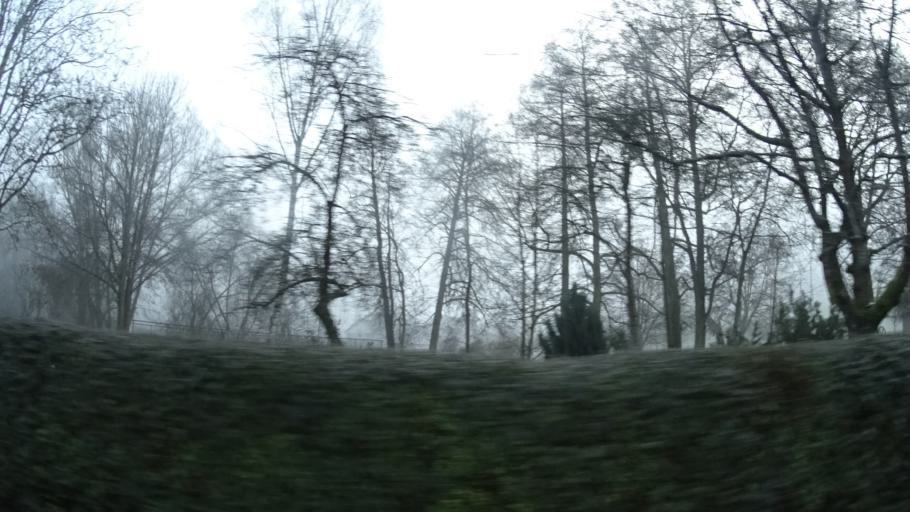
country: DE
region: Bavaria
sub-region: Regierungsbezirk Unterfranken
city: Neunkirchen
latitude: 49.6712
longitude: 9.3756
